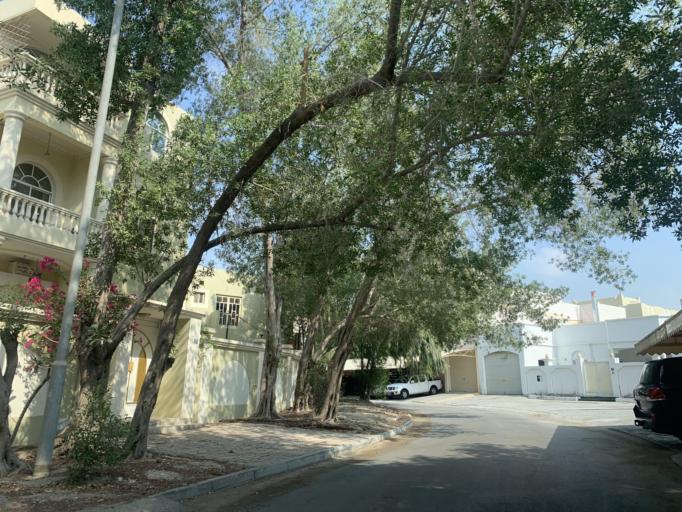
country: BH
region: Central Governorate
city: Madinat Hamad
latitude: 26.1061
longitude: 50.5039
